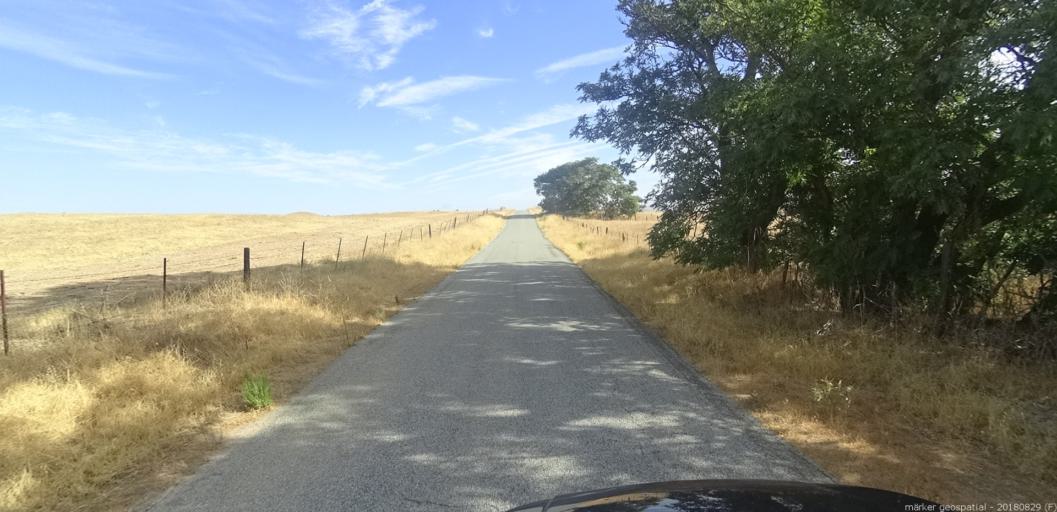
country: US
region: California
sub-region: Monterey County
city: King City
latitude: 36.0206
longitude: -120.9486
